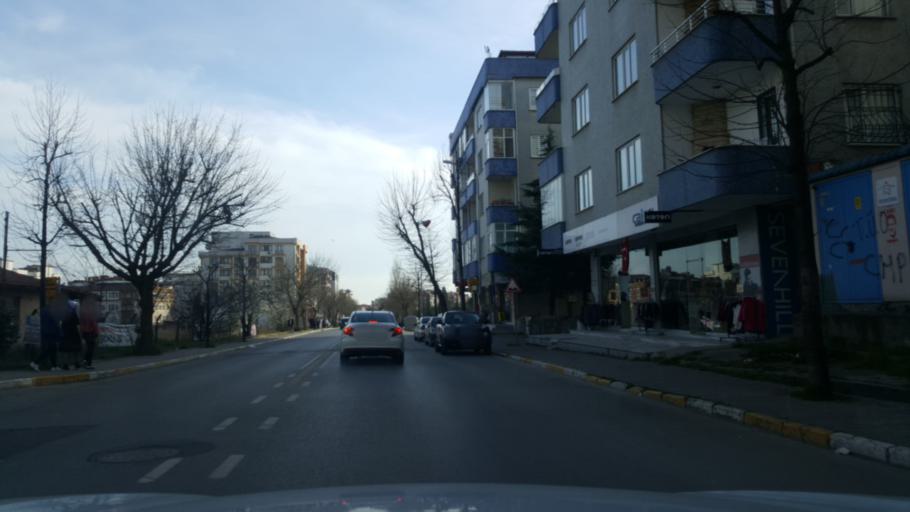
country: TR
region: Istanbul
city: Icmeler
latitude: 40.8247
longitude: 29.3103
